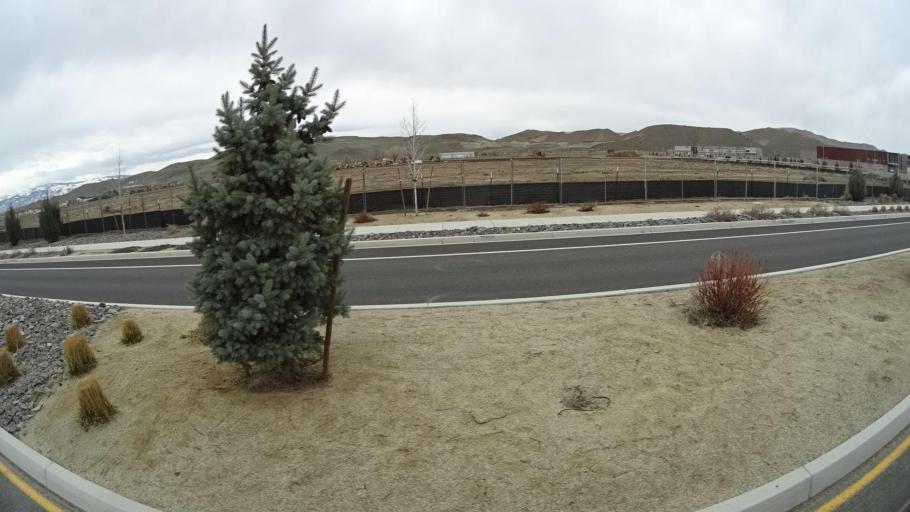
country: US
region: Nevada
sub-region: Washoe County
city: Spanish Springs
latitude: 39.6078
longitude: -119.7218
